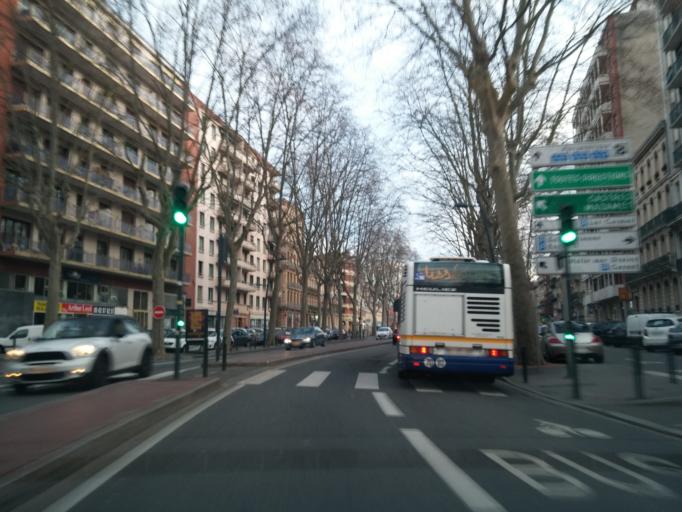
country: FR
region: Midi-Pyrenees
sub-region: Departement de la Haute-Garonne
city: Toulouse
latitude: 43.6026
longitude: 1.4516
